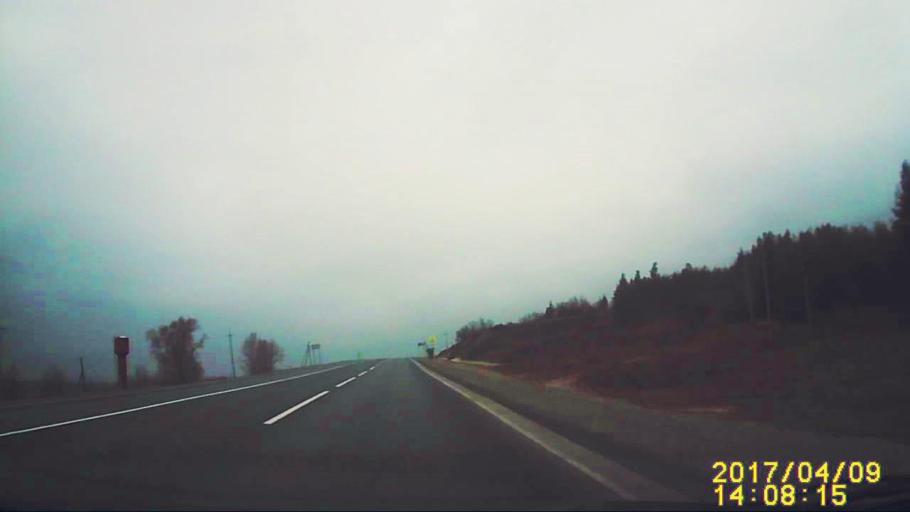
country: RU
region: Ulyanovsk
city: Silikatnyy
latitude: 54.0186
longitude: 48.2160
